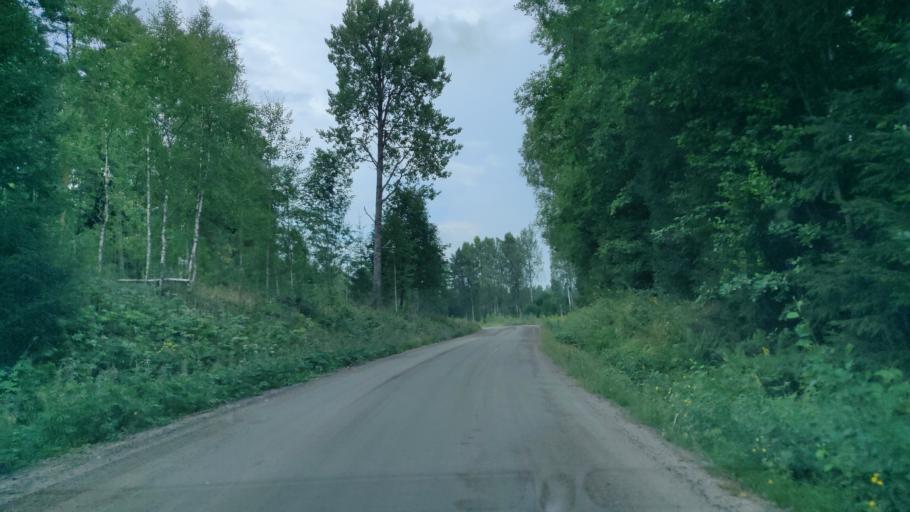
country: SE
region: Vaermland
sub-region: Munkfors Kommun
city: Munkfors
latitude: 59.9605
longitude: 13.4926
